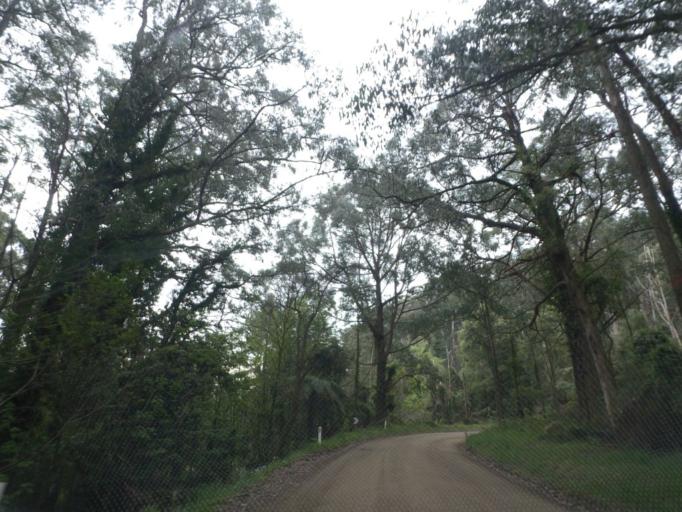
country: AU
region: Victoria
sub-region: Yarra Ranges
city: Olinda
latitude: -37.8566
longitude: 145.3427
